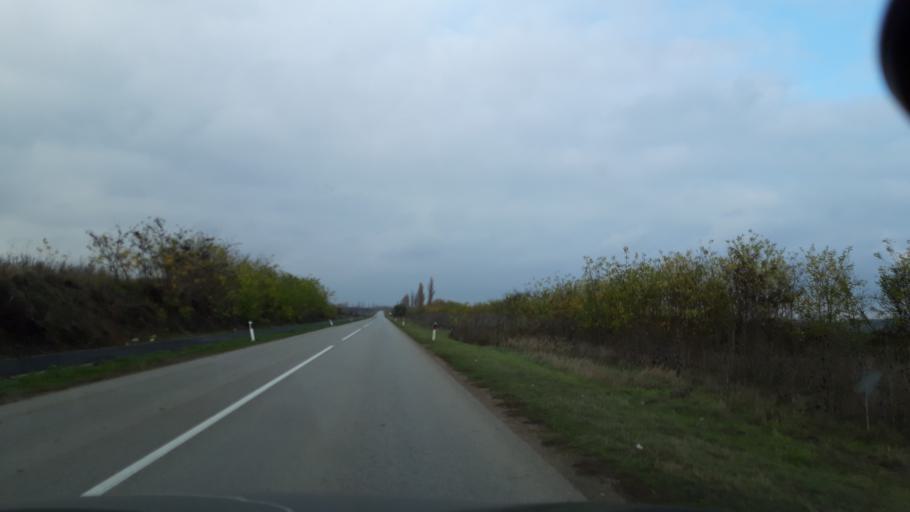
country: RS
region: Autonomna Pokrajina Vojvodina
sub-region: Severnobanatski Okrug
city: Novi Knezevac
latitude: 46.0648
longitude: 20.1034
